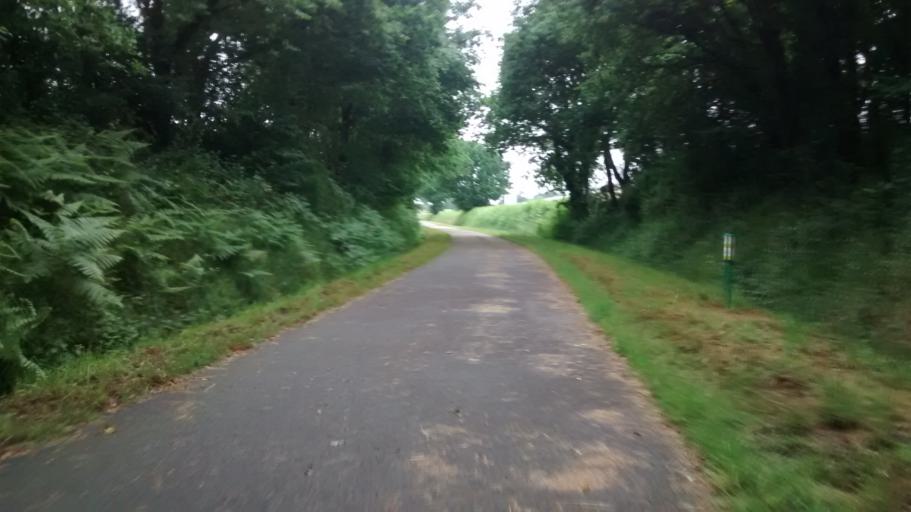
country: FR
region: Brittany
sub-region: Departement du Morbihan
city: Malestroit
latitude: 47.7865
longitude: -2.3917
